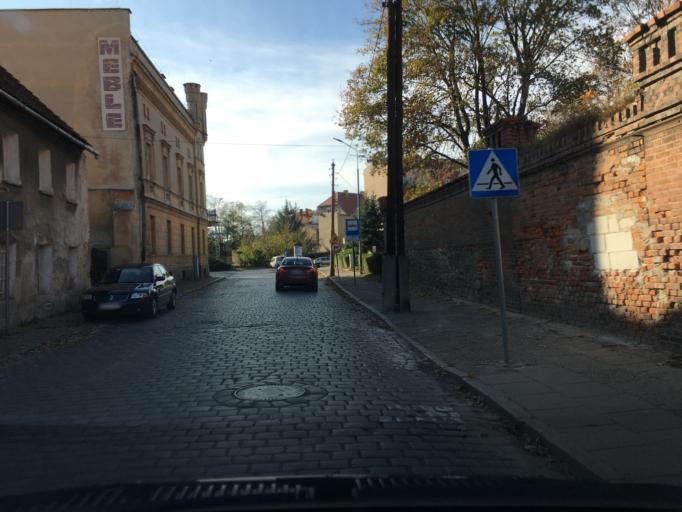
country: PL
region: Lower Silesian Voivodeship
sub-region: Powiat strzelinski
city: Strzelin
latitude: 50.7794
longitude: 17.0734
